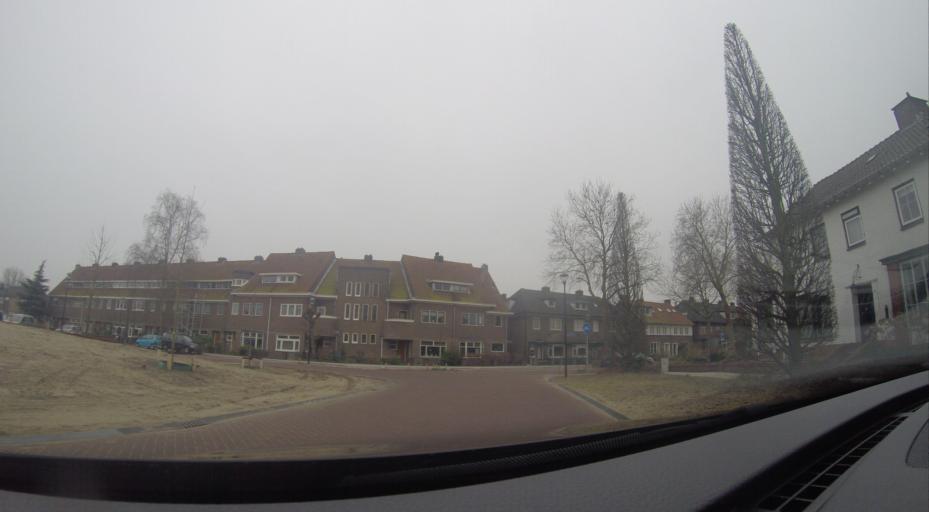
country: NL
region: Gelderland
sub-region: Gemeente Zutphen
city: Zutphen
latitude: 52.1516
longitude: 6.2117
